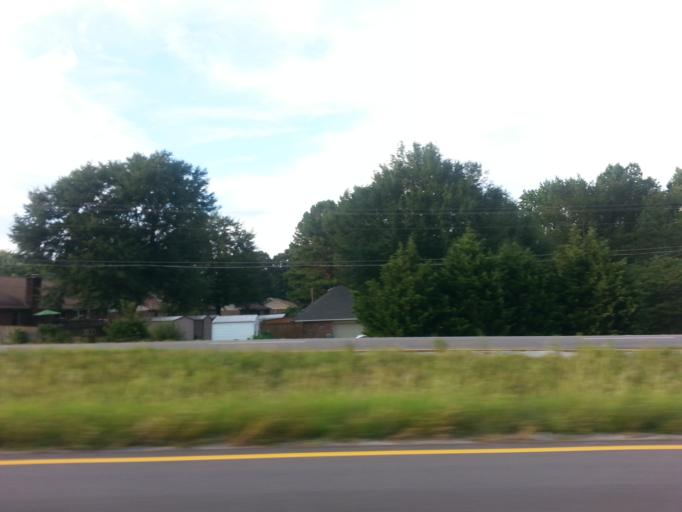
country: US
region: Alabama
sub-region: Madison County
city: Madison
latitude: 34.7483
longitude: -86.7908
